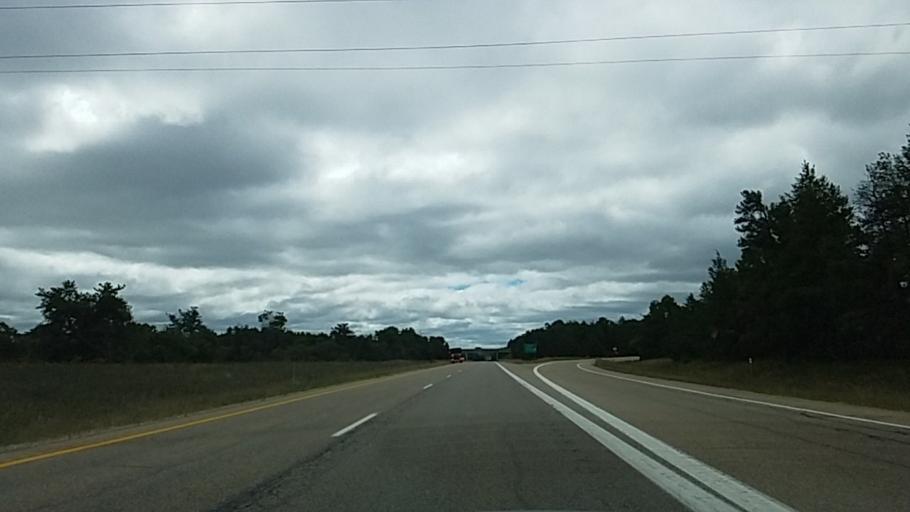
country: US
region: Michigan
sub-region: Crawford County
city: Grayling
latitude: 44.6747
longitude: -84.6960
